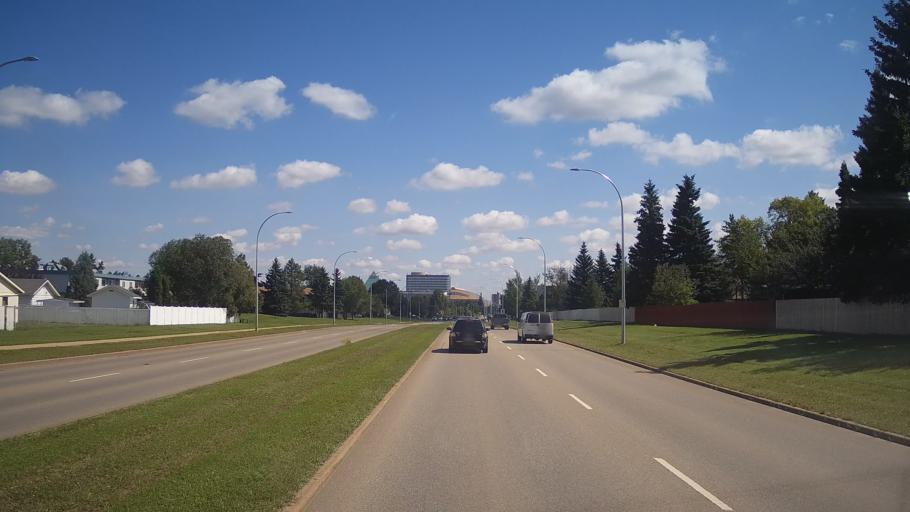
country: CA
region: Alberta
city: St. Albert
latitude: 53.5215
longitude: -113.6425
